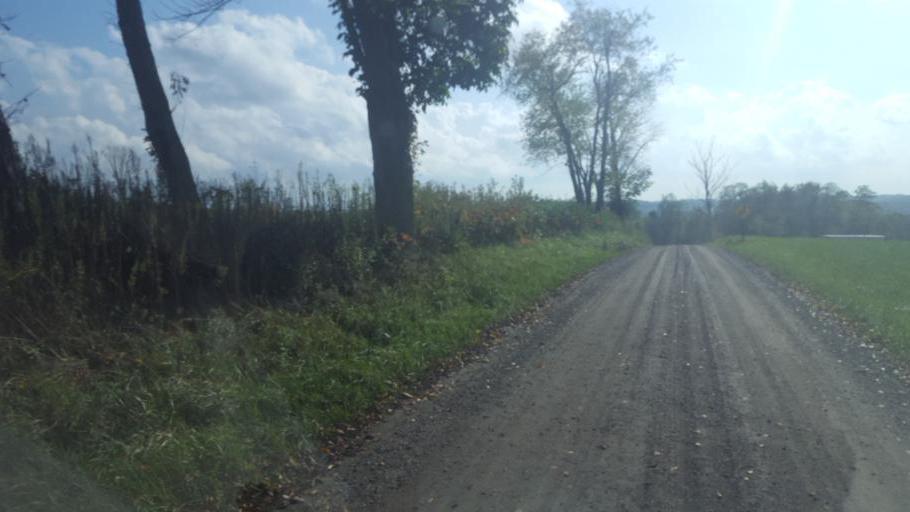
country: US
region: Ohio
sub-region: Holmes County
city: Millersburg
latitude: 40.6265
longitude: -81.8732
